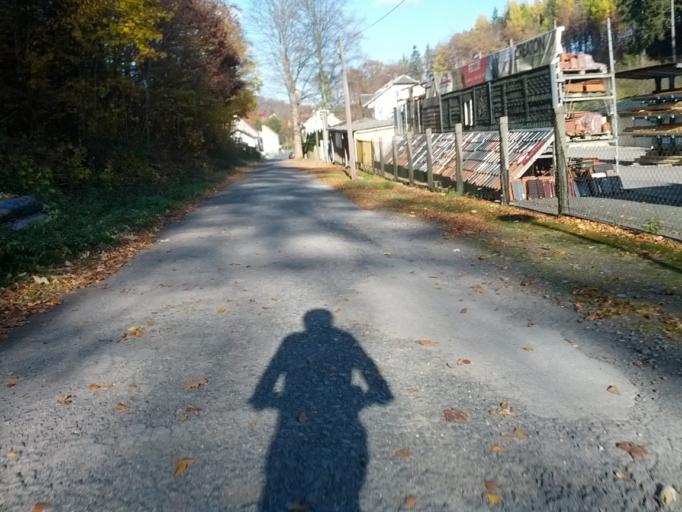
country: DE
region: Thuringia
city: Thal
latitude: 50.9099
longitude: 10.3998
